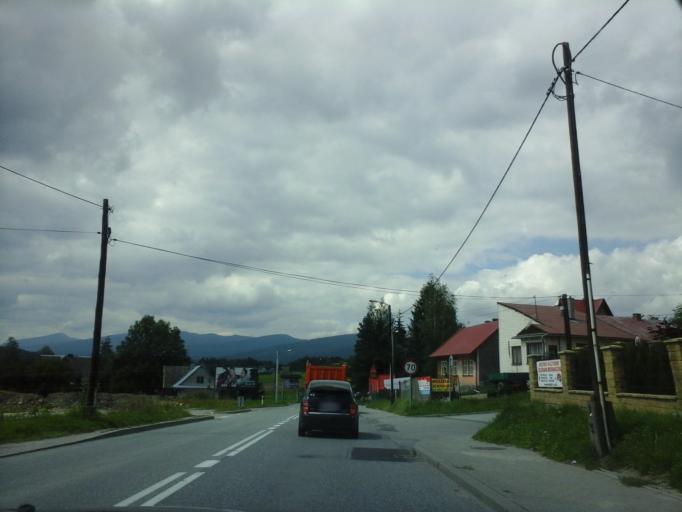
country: PL
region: Lesser Poland Voivodeship
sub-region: Powiat suski
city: Jordanow
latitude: 49.6519
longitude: 19.8231
